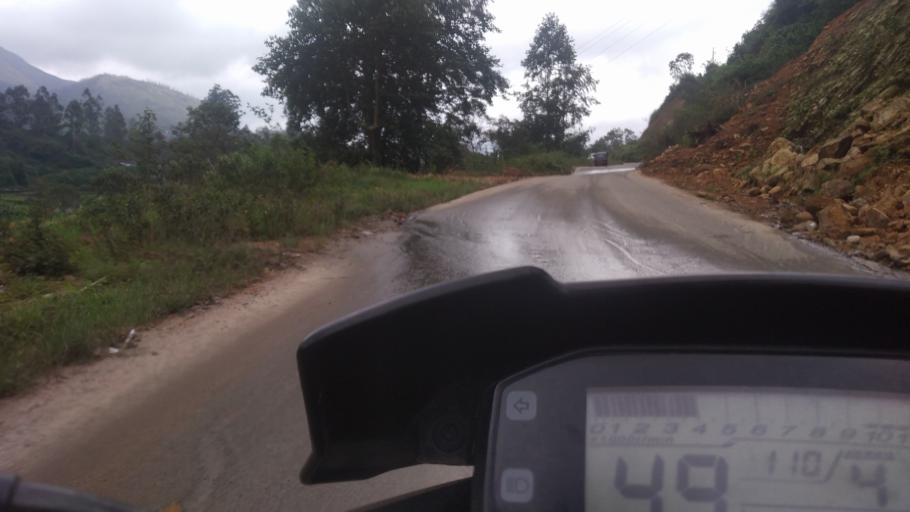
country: IN
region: Kerala
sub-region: Idukki
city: Munnar
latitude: 10.0839
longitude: 77.0671
